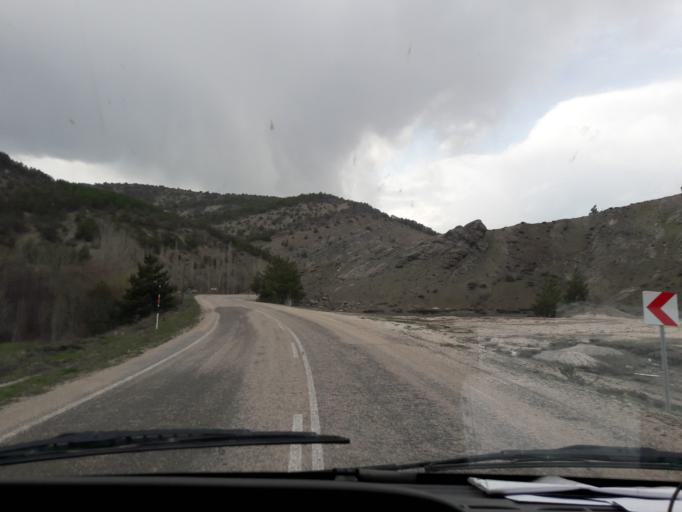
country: TR
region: Giresun
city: Alucra
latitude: 40.2814
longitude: 38.8208
